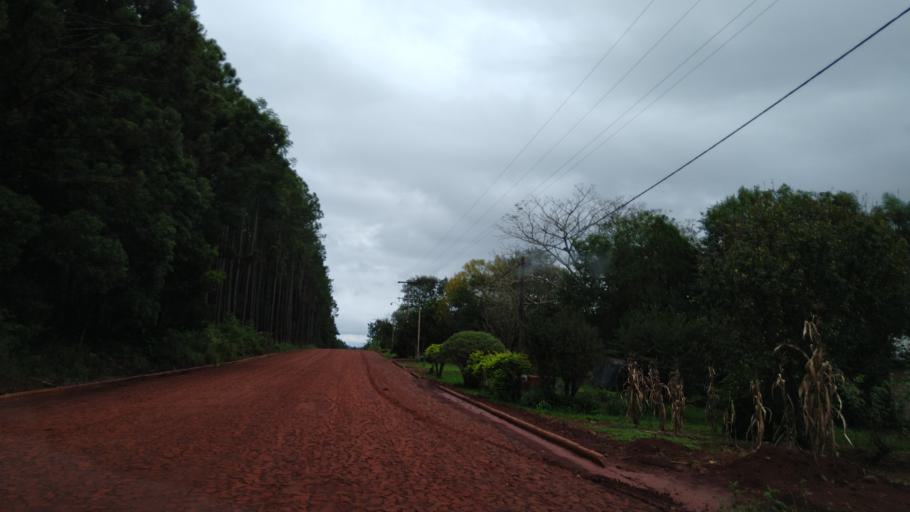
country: AR
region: Misiones
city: Capiovi
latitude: -26.9350
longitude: -55.0395
